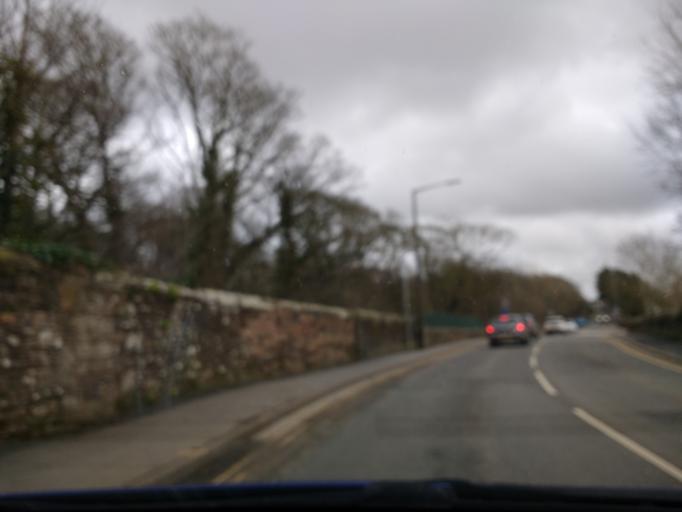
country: GB
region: England
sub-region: Cumbria
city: Maryport
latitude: 54.7142
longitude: -3.4928
